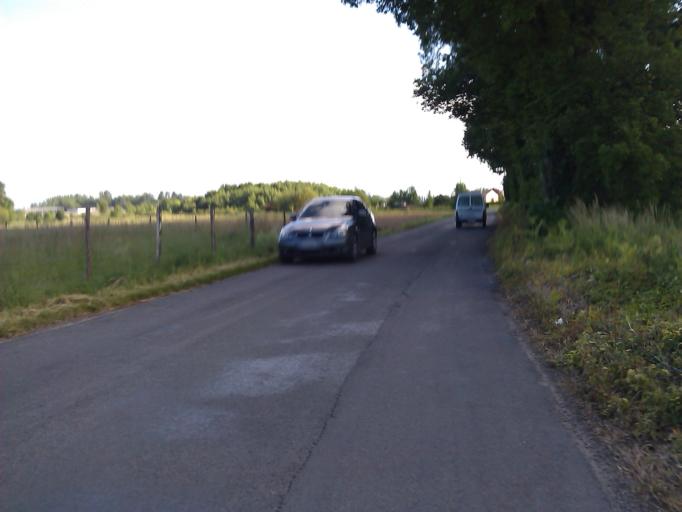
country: FR
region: Aquitaine
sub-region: Departement de la Gironde
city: Saint-Gervais
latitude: 45.0231
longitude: -0.4418
